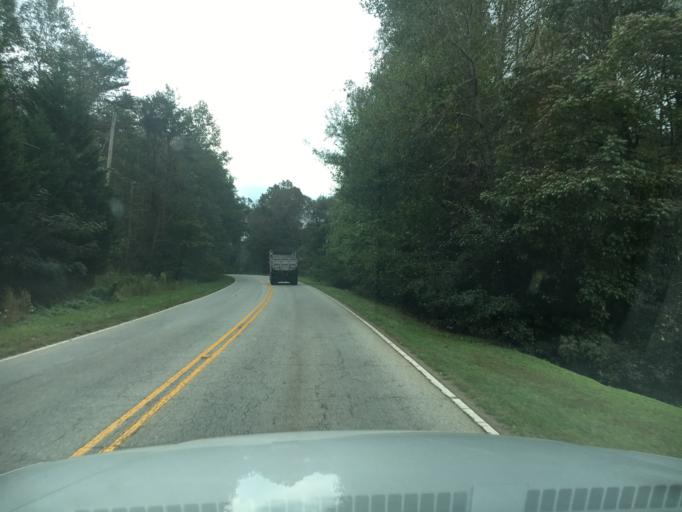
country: US
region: South Carolina
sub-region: Greenville County
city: Greer
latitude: 35.0055
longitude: -82.2562
